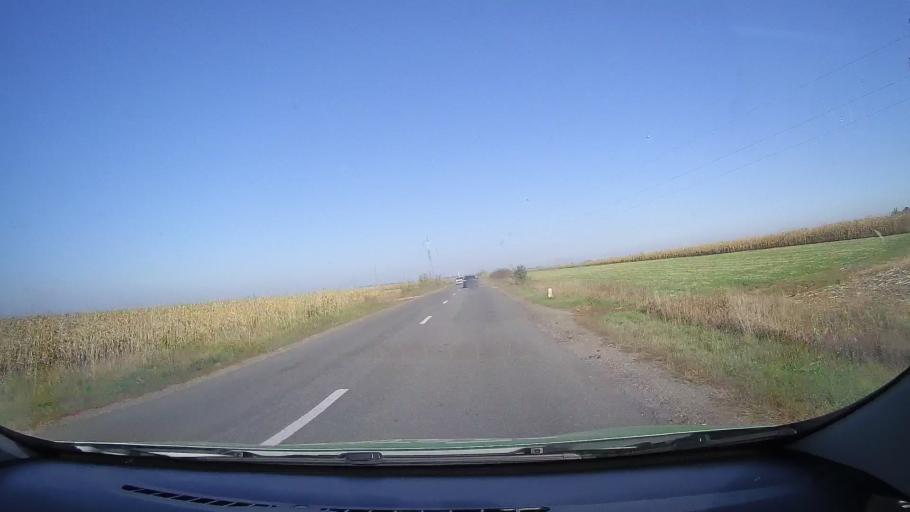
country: RO
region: Satu Mare
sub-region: Comuna Cauas
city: Cauas
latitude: 47.6064
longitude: 22.5417
